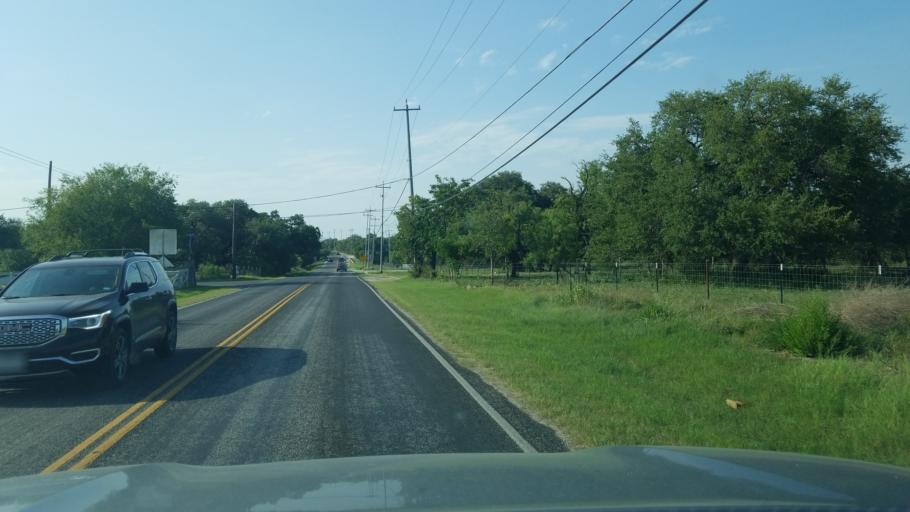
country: US
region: Texas
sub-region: Bexar County
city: Leon Valley
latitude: 29.4487
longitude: -98.7534
